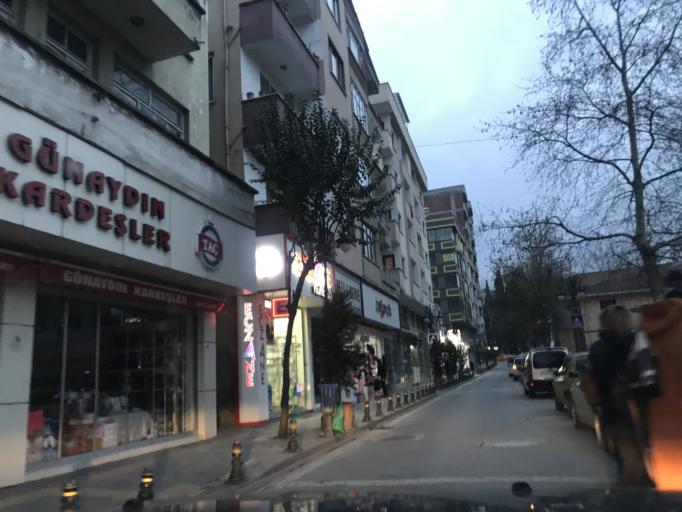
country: TR
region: Trabzon
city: Akcaabat
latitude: 41.0231
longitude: 39.5670
